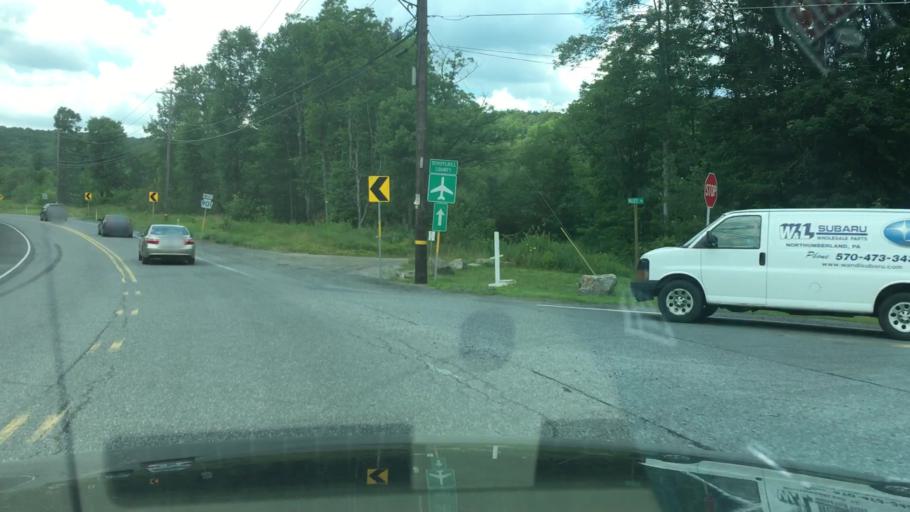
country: US
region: Pennsylvania
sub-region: Schuylkill County
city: Minersville
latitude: 40.7098
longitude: -76.3311
